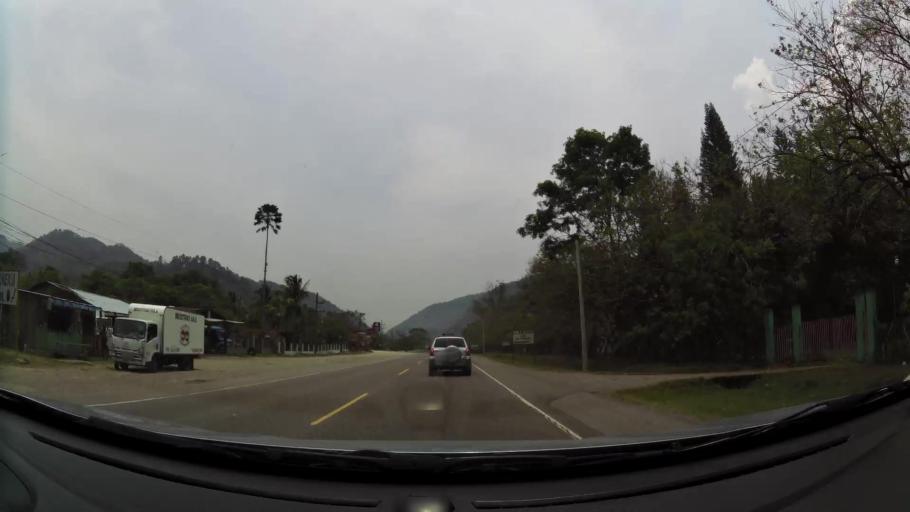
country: HN
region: Comayagua
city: Taulabe
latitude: 14.7161
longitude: -87.9659
